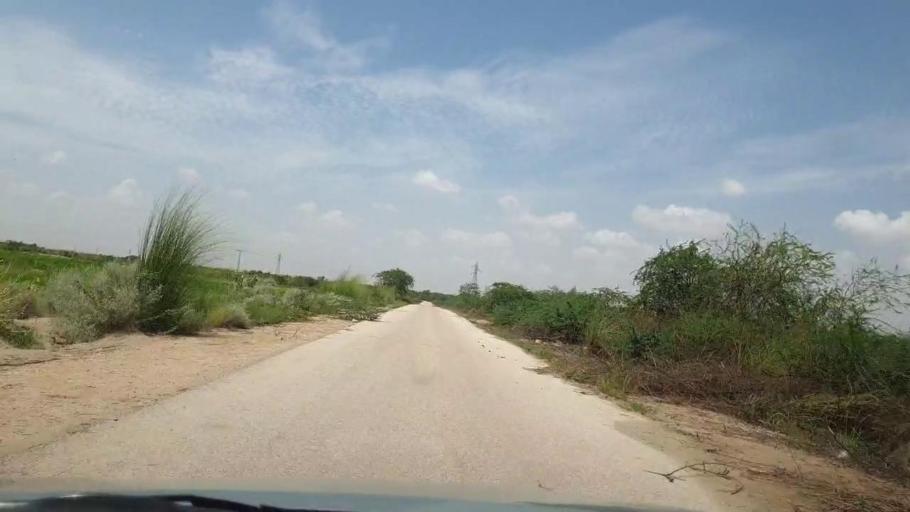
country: PK
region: Sindh
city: Bozdar
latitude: 27.0252
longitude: 68.9394
